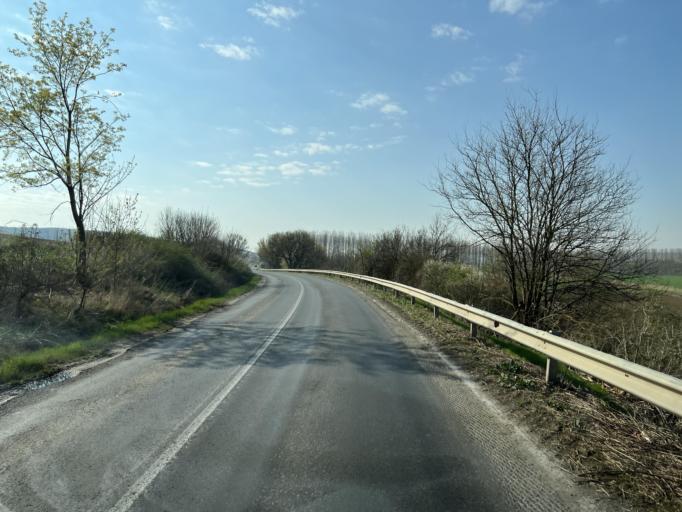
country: HU
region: Pest
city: Galgamacsa
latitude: 47.7317
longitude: 19.3745
